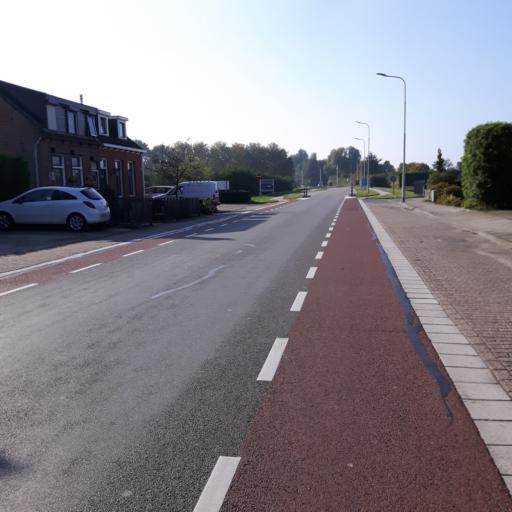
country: NL
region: Zeeland
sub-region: Gemeente Goes
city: Goes
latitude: 51.4810
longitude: 3.9459
